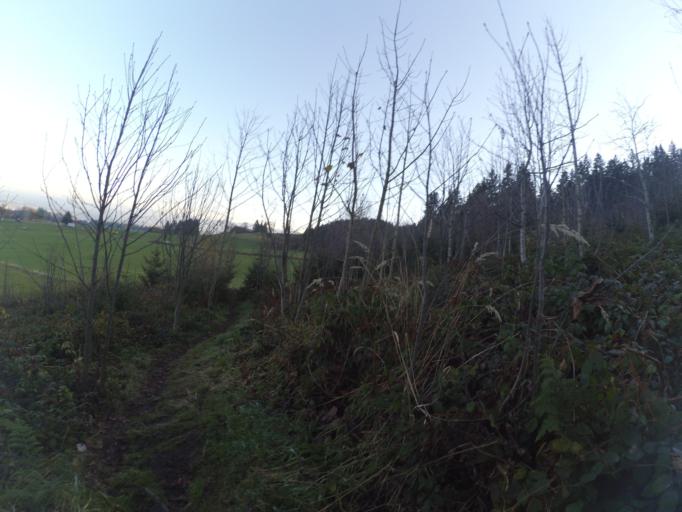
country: DE
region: Bavaria
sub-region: Upper Bavaria
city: Bernbeuren
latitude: 47.7378
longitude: 10.7404
